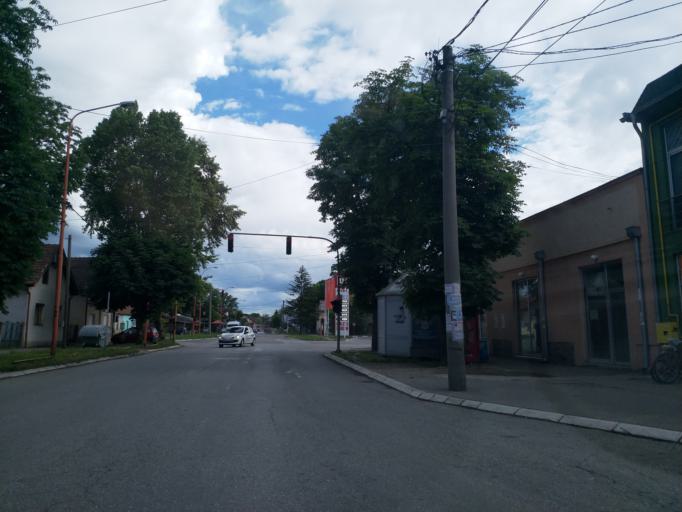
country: RS
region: Central Serbia
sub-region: Pomoravski Okrug
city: Cuprija
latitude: 43.9205
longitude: 21.3743
